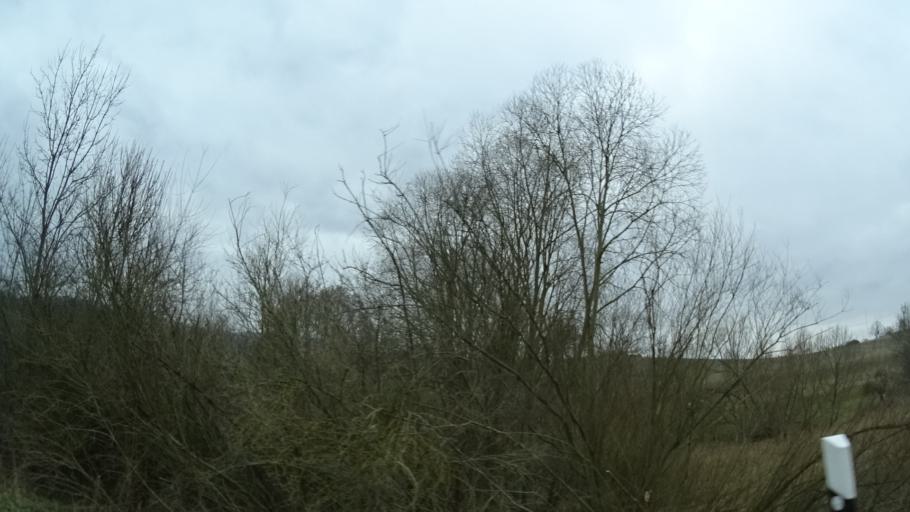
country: DE
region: Thuringia
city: Bad Blankenburg
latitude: 50.7030
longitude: 11.2269
